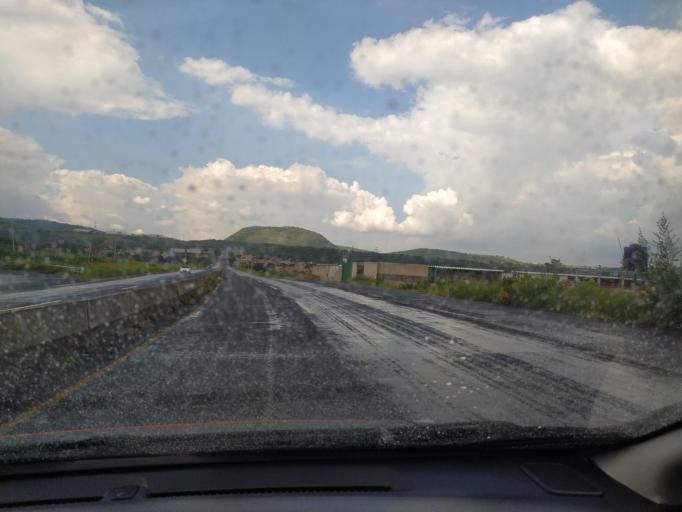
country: MX
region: Jalisco
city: Bellavista
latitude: 20.4240
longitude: -103.6082
